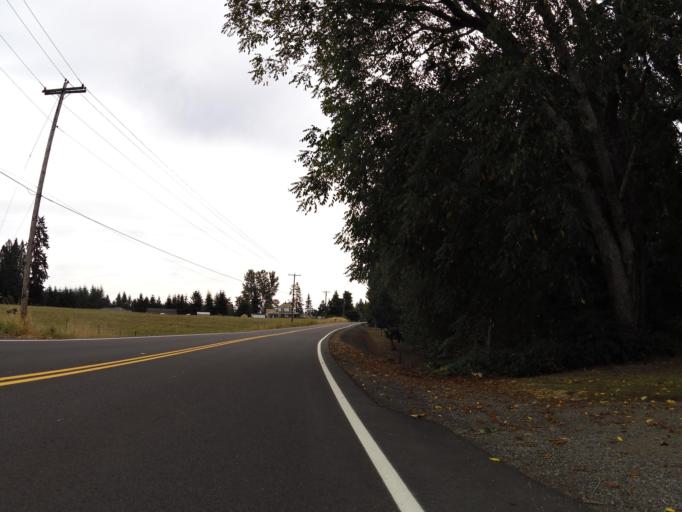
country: US
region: Washington
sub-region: Cowlitz County
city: Castle Rock
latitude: 46.2306
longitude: -122.8915
